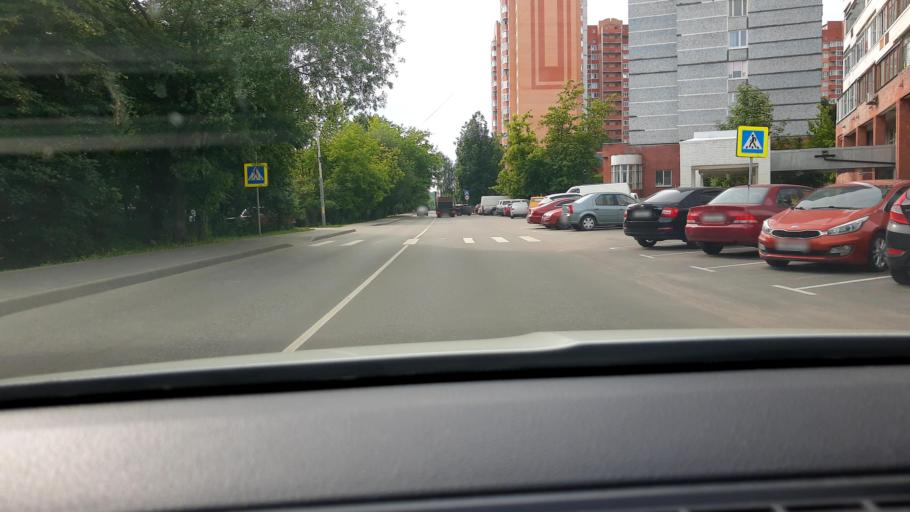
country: RU
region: Moskovskaya
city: Troitsk
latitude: 55.4877
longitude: 37.3065
